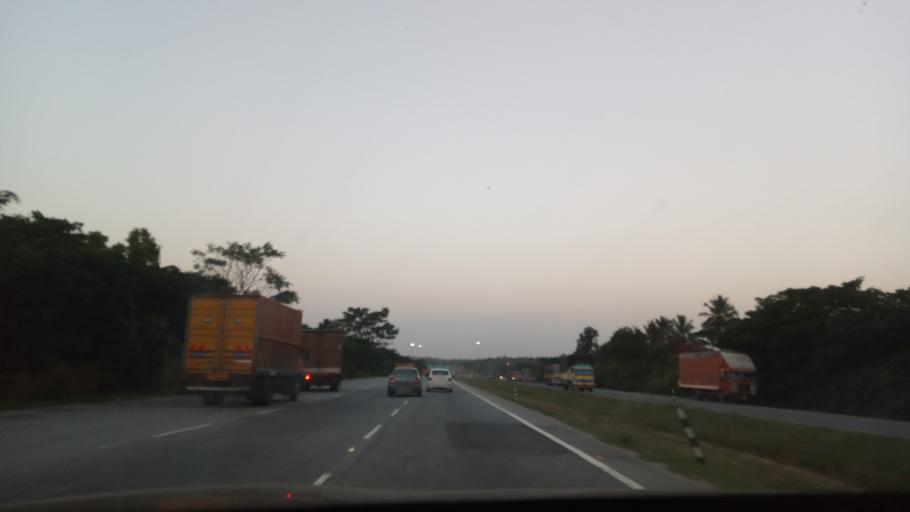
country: IN
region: Karnataka
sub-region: Bangalore Rural
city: Nelamangala
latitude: 13.0490
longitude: 77.4759
